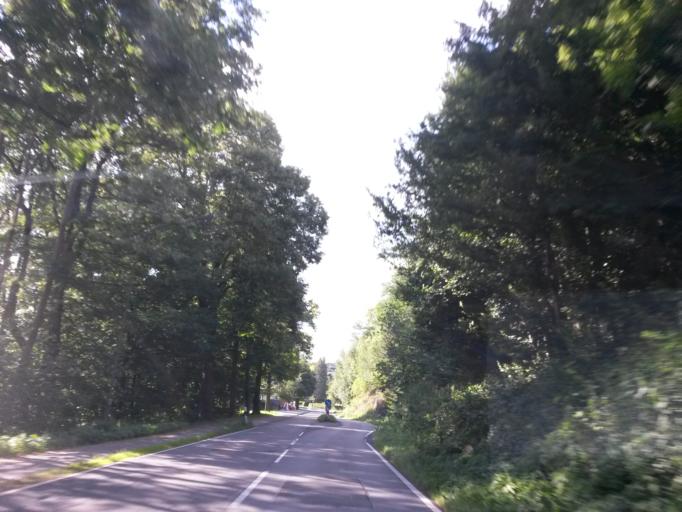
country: DE
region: North Rhine-Westphalia
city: Waldbrol
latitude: 50.8978
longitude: 7.6280
